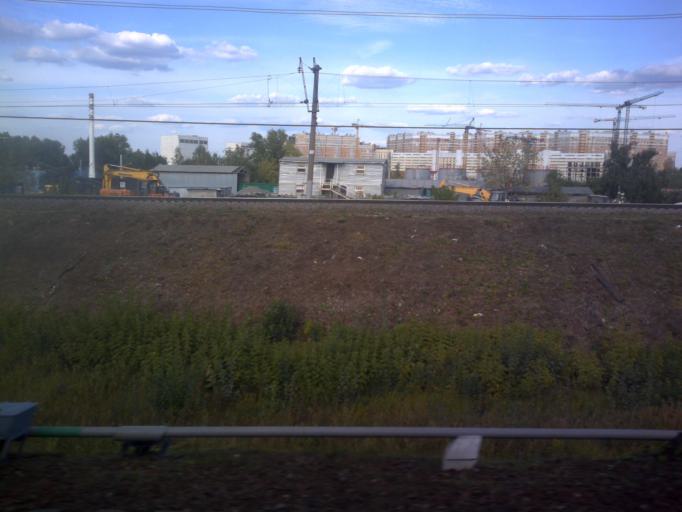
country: RU
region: Moskovskaya
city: Biryulevo Zapadnoye
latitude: 55.6031
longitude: 37.6474
